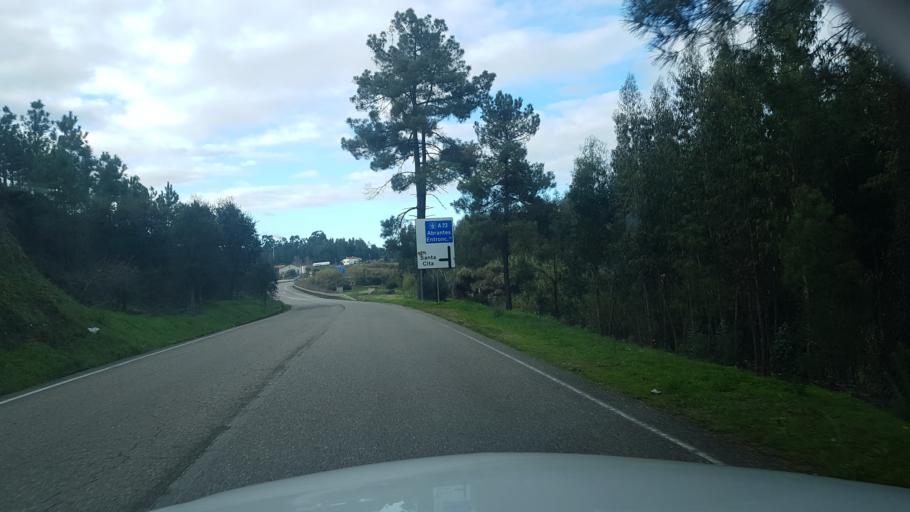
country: PT
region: Santarem
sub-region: Constancia
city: Constancia
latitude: 39.4801
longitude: -8.3512
